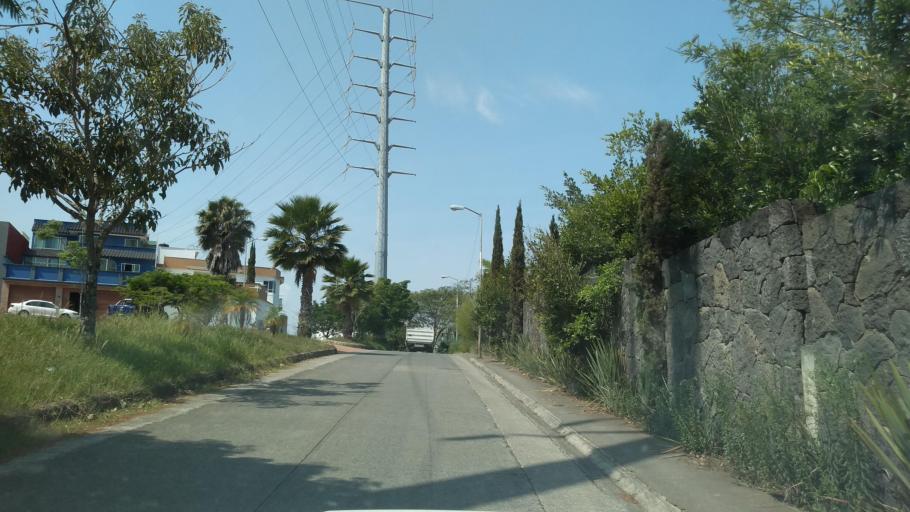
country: MX
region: Veracruz
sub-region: Emiliano Zapata
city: Las Trancas
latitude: 19.5246
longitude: -96.8656
